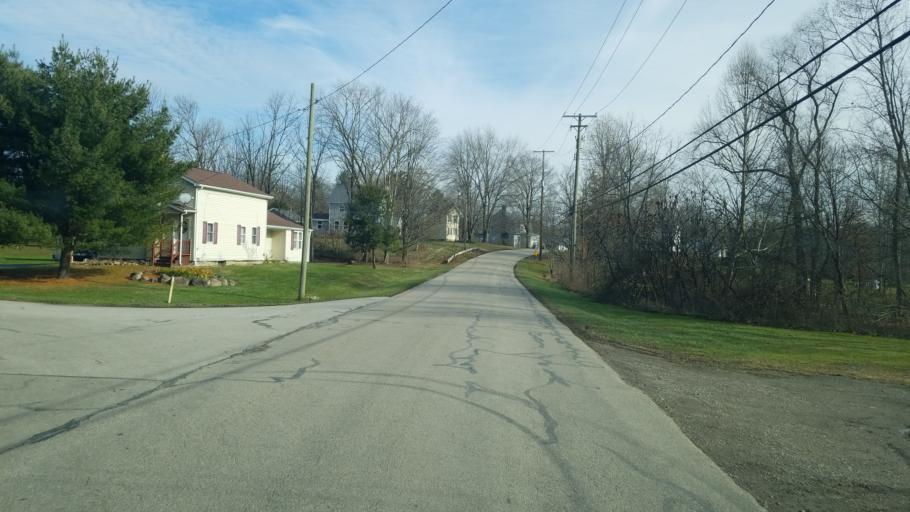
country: US
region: Ohio
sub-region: Ashtabula County
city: Roaming Shores
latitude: 41.6607
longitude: -80.8559
